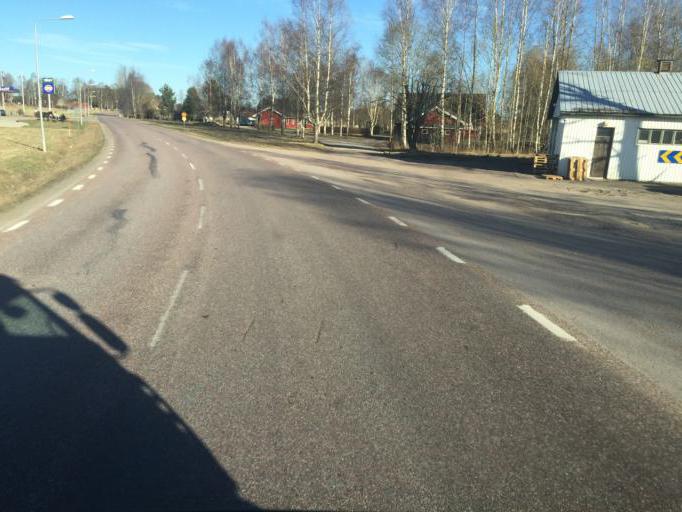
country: SE
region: Dalarna
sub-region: Vansbro Kommun
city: Jarna
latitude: 60.4530
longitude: 14.4979
